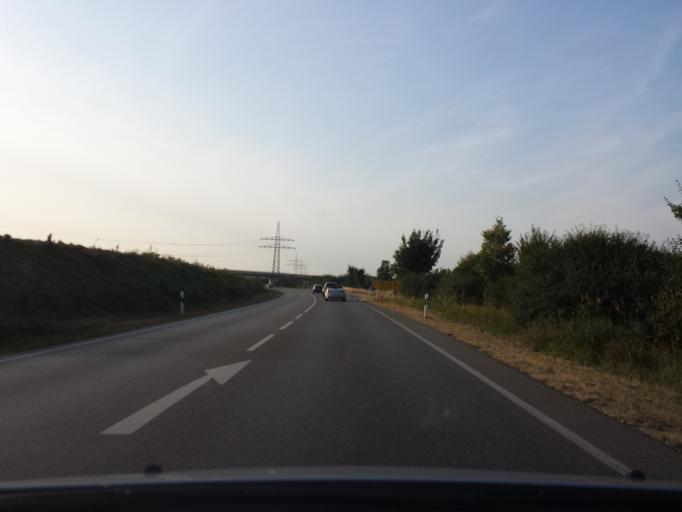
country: DE
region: Bavaria
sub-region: Swabia
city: Friedberg
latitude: 48.3807
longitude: 10.9615
